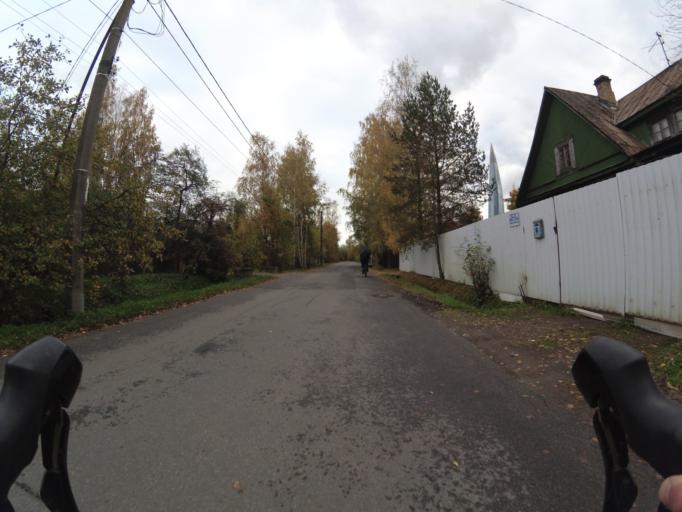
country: RU
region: St.-Petersburg
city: Lakhtinskiy
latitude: 59.9940
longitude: 30.1621
